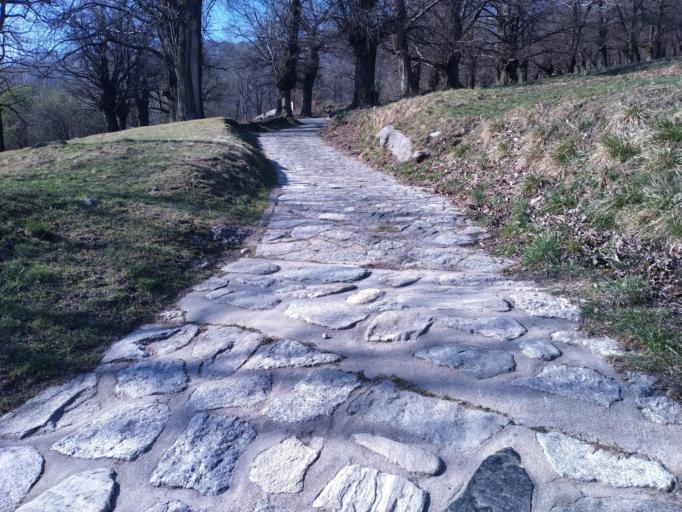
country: IT
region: Lombardy
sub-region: Provincia di Como
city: Caglio
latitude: 45.8592
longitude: 9.2387
